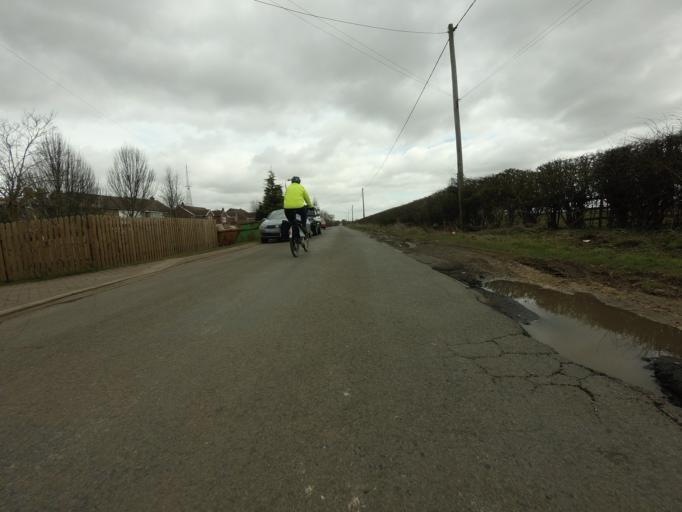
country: GB
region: England
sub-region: Lincolnshire
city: Grantham
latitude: 52.8903
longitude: -0.6567
